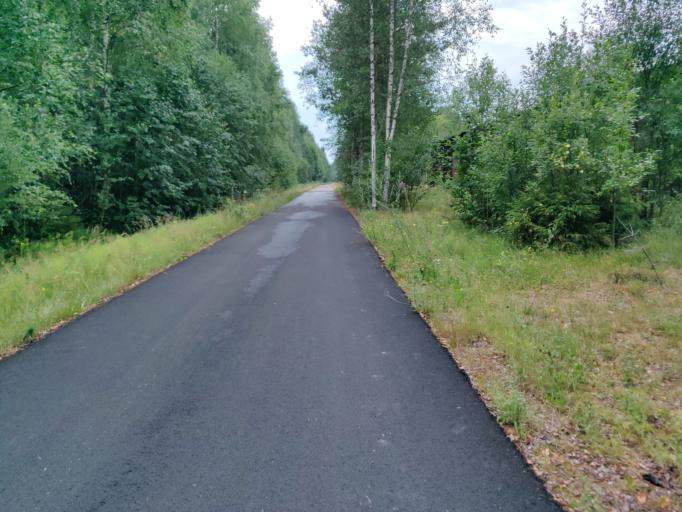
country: SE
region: Vaermland
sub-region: Hagfors Kommun
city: Hagfors
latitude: 59.9677
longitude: 13.5720
